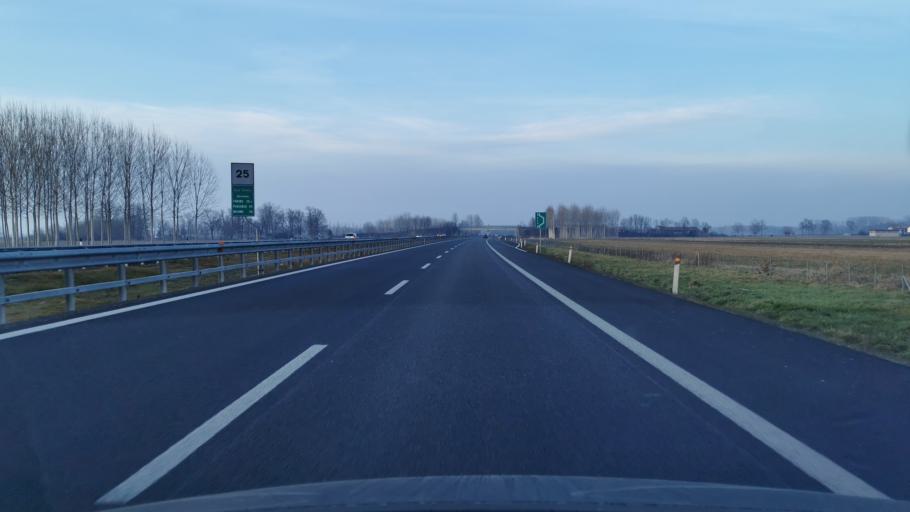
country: IT
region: Piedmont
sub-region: Provincia di Cuneo
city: Caramagna Piemonte
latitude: 44.7463
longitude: 7.7514
